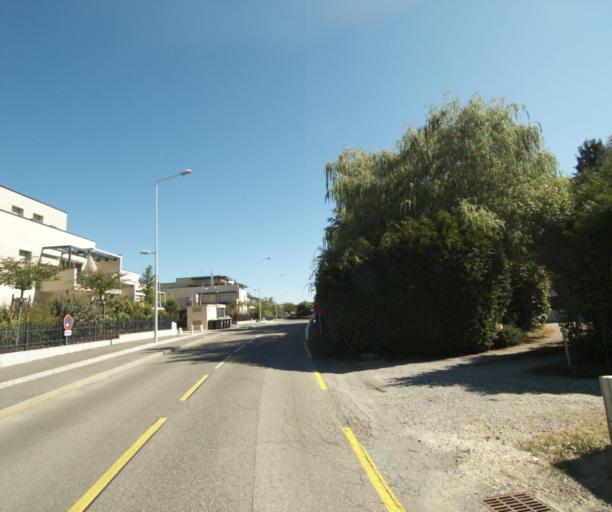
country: FR
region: Rhone-Alpes
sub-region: Departement de l'Ain
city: Ornex
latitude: 46.2690
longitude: 6.0972
